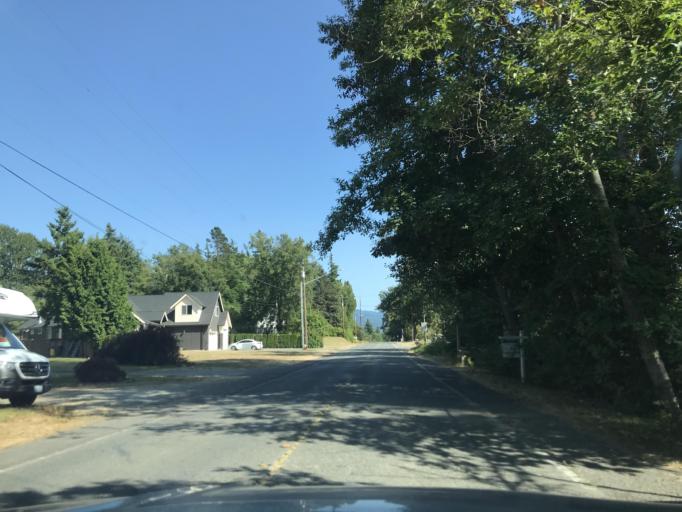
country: US
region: Washington
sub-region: Whatcom County
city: Bellingham
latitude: 48.7841
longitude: -122.5134
